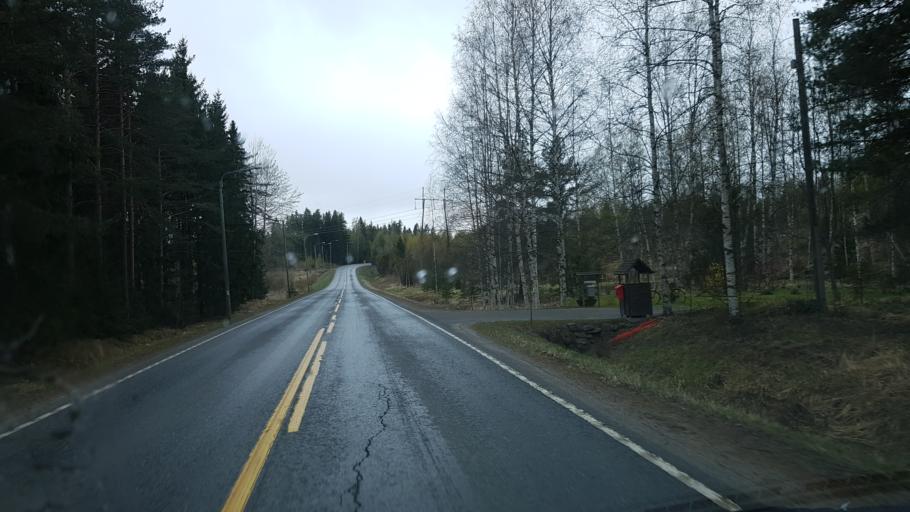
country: FI
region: Pirkanmaa
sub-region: Tampere
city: Pirkkala
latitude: 61.4287
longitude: 23.6286
